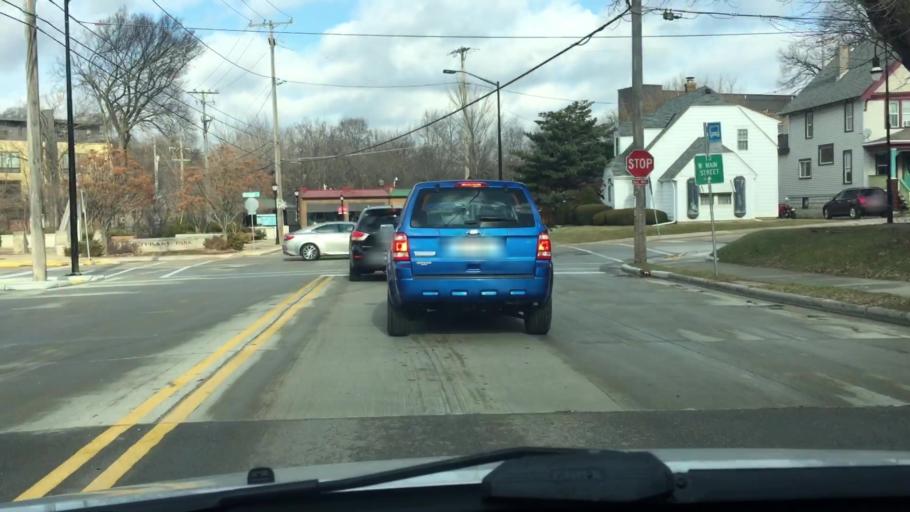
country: US
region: Wisconsin
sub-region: Waukesha County
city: Waukesha
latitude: 43.0094
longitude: -88.2365
